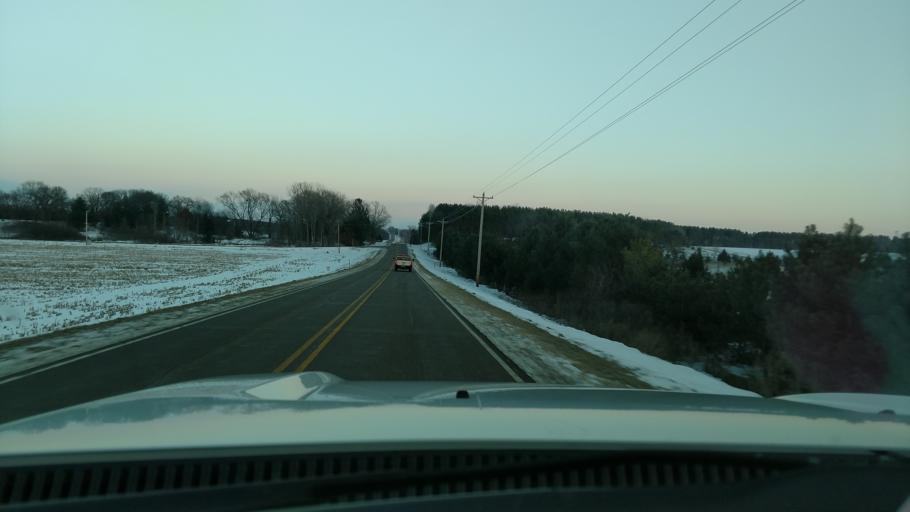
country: US
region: Wisconsin
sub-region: Saint Croix County
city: Roberts
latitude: 44.9132
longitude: -92.5107
